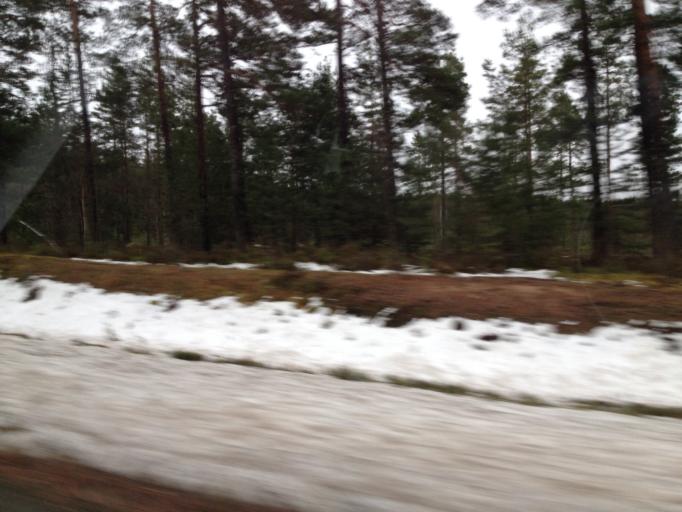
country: FI
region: Uusimaa
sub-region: Raaseporin
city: Hanko
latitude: 59.8625
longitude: 23.0533
